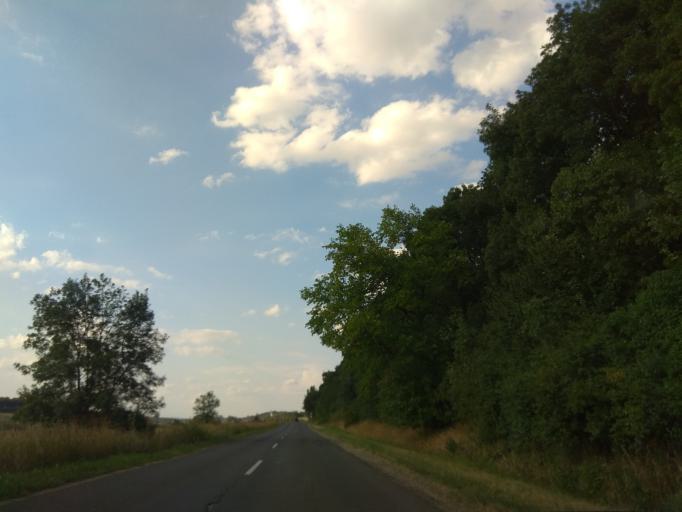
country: HU
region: Borsod-Abauj-Zemplen
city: Harsany
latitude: 47.9442
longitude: 20.7442
